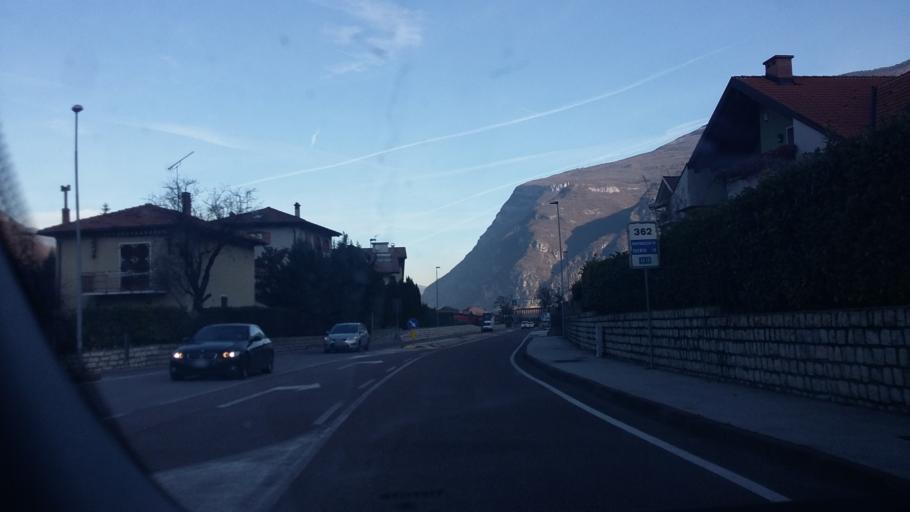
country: IT
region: Trentino-Alto Adige
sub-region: Provincia di Trento
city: Calliano
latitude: 45.9297
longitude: 11.0928
